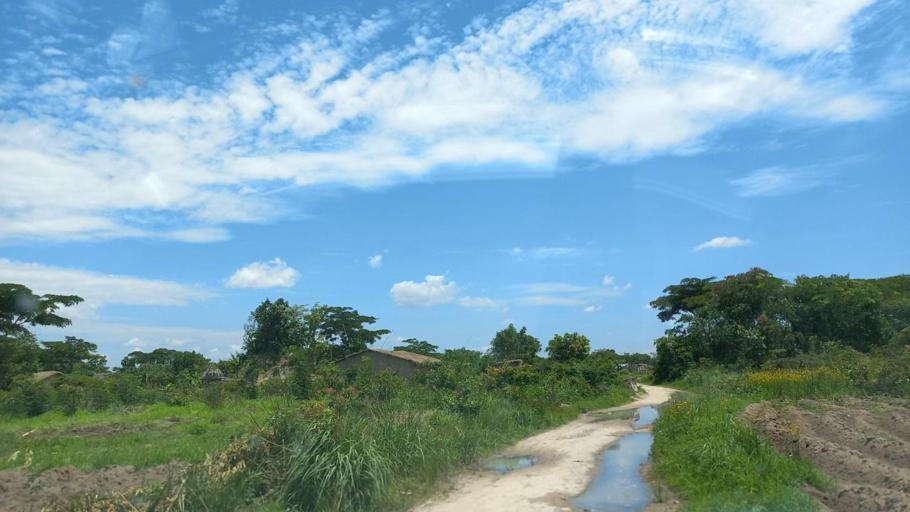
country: ZM
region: Copperbelt
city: Ndola
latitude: -12.8690
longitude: 28.4415
